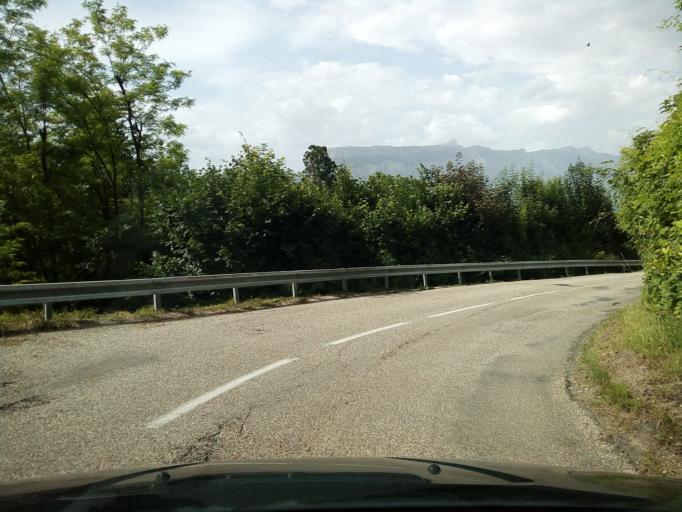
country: FR
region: Rhone-Alpes
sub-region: Departement de l'Isere
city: Saint-Martin-d'Heres
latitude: 45.1693
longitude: 5.7727
